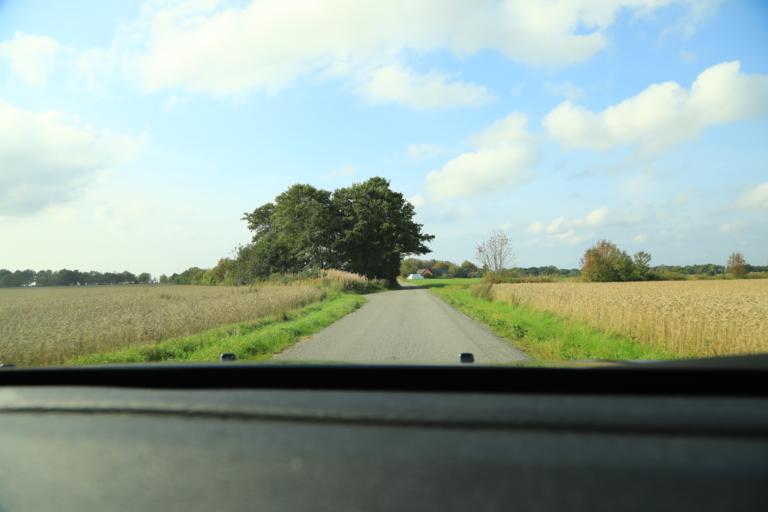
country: SE
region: Halland
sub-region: Varbergs Kommun
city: Tvaaker
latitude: 57.0095
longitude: 12.3720
